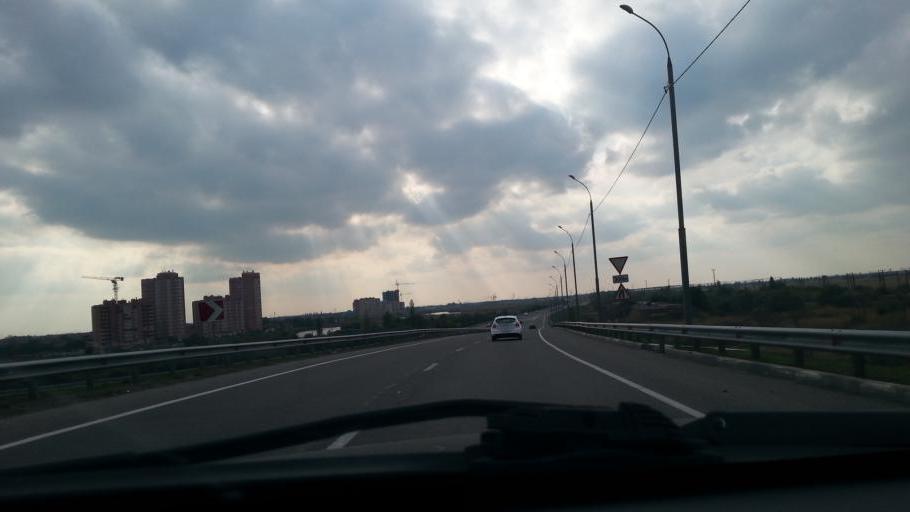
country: RU
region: Rostov
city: Bataysk
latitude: 47.1589
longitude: 39.7360
